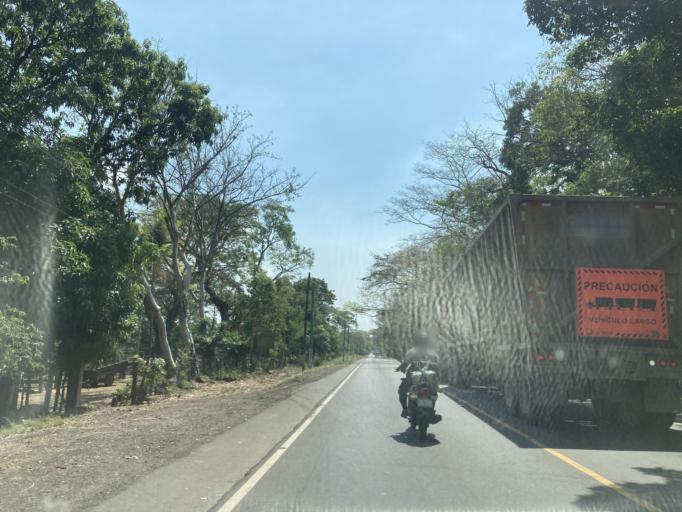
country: GT
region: Escuintla
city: Guanagazapa
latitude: 14.2118
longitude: -90.7225
